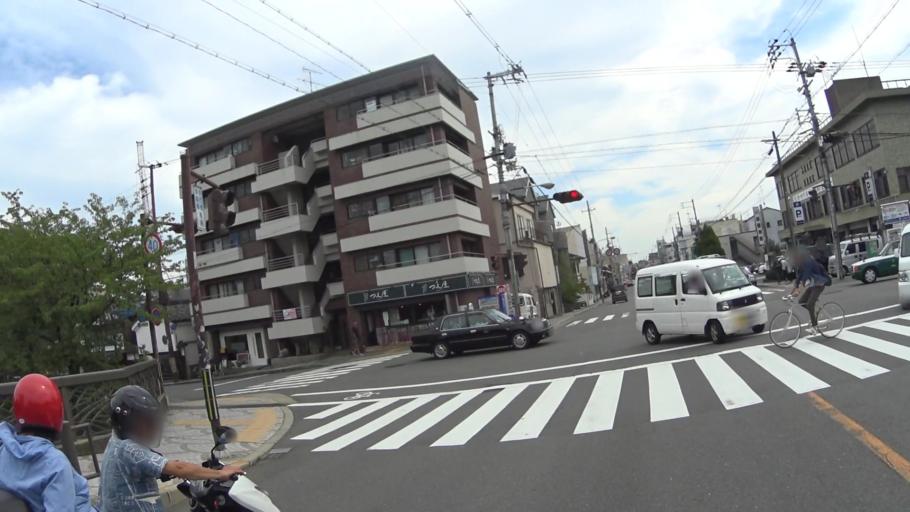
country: JP
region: Kyoto
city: Kyoto
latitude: 35.0156
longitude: 135.7784
